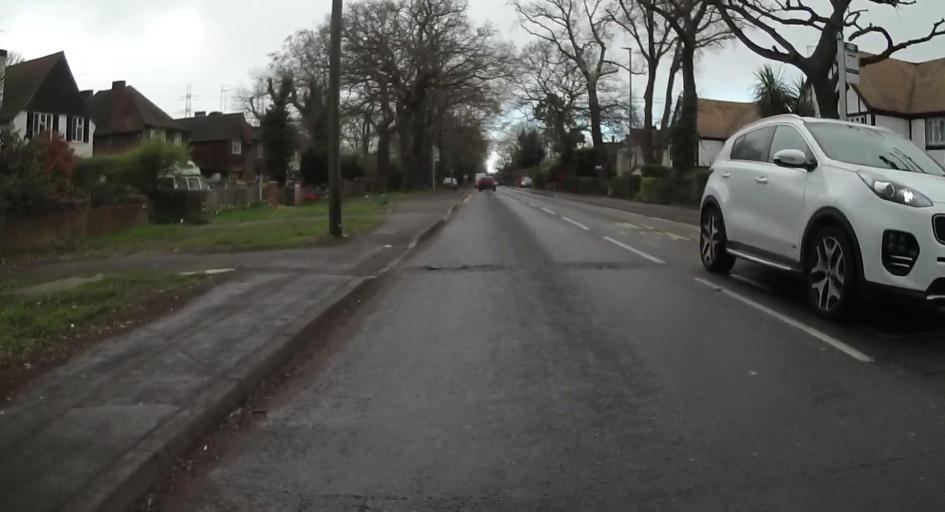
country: GB
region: England
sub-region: Surrey
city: Byfleet
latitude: 51.3500
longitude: -0.4823
